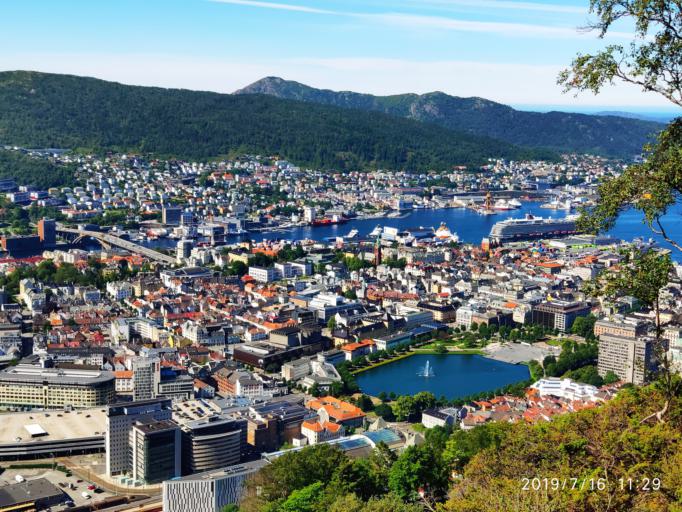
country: NO
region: Hordaland
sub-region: Bergen
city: Bergen
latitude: 60.3919
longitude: 5.3470
